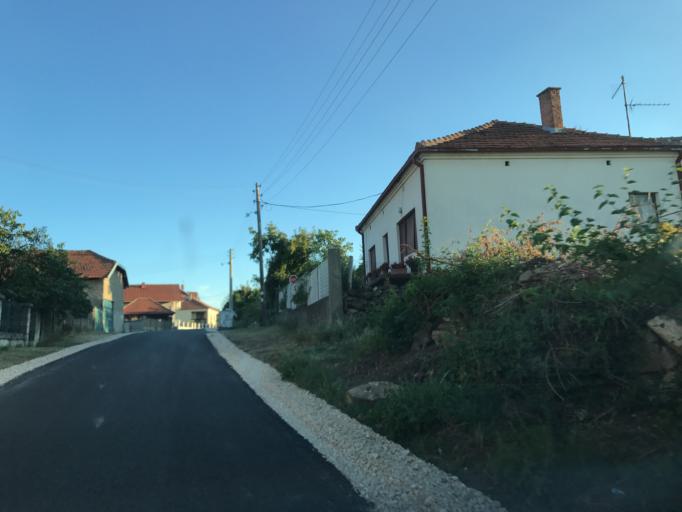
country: BG
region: Vidin
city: Bregovo
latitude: 44.1273
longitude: 22.5993
